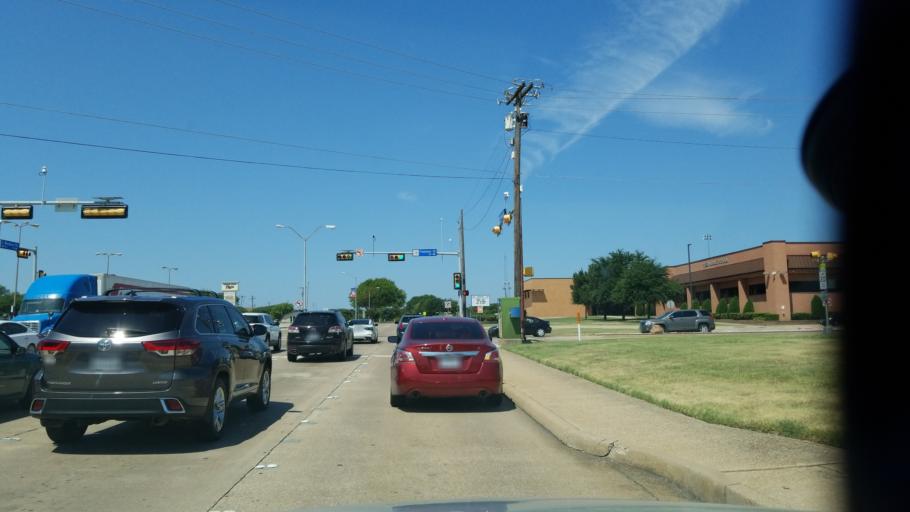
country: US
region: Texas
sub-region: Dallas County
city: Duncanville
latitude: 32.6475
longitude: -96.8995
